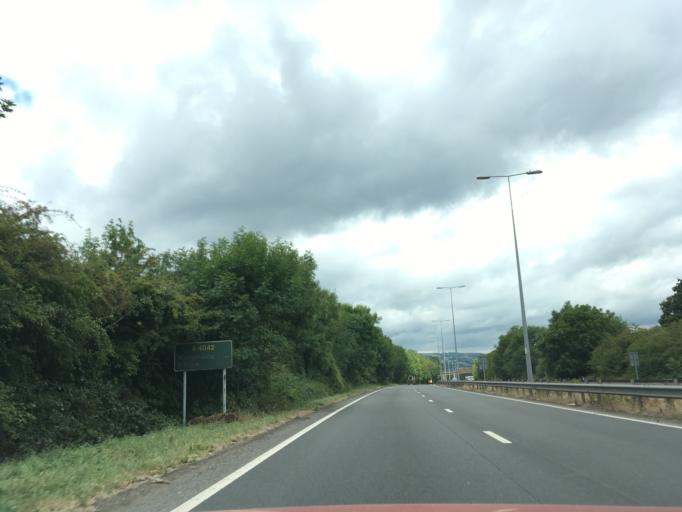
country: GB
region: Wales
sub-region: Torfaen County Borough
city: New Inn
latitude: 51.6697
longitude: -3.0068
